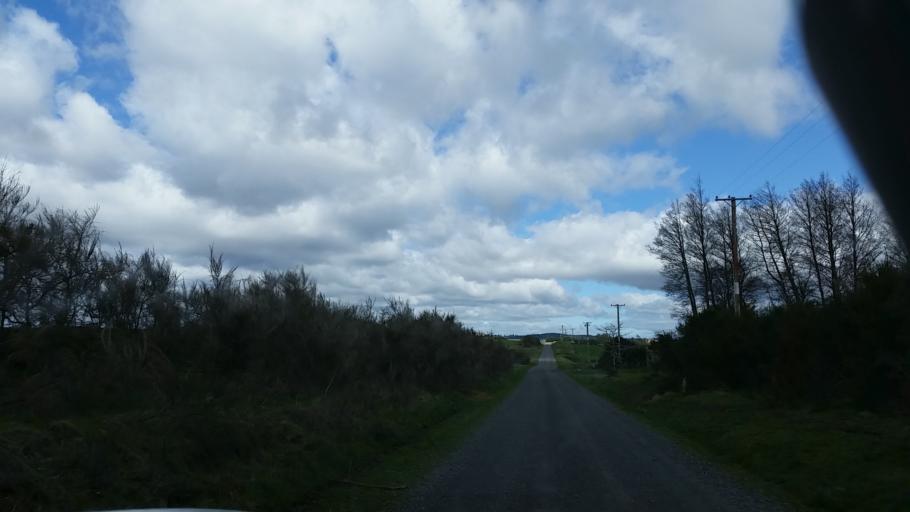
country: NZ
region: Bay of Plenty
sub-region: Whakatane District
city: Murupara
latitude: -38.3063
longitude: 176.5596
